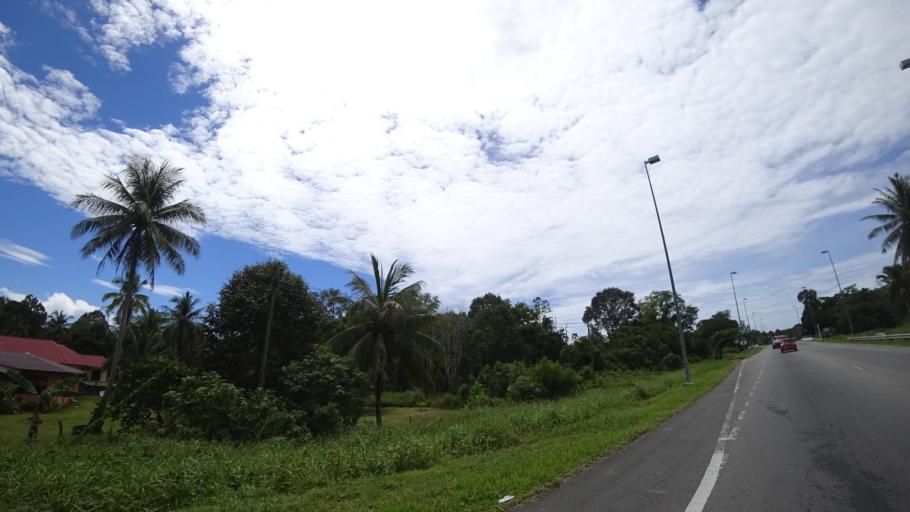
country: BN
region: Brunei and Muara
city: Bandar Seri Begawan
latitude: 4.8070
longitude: 114.8328
